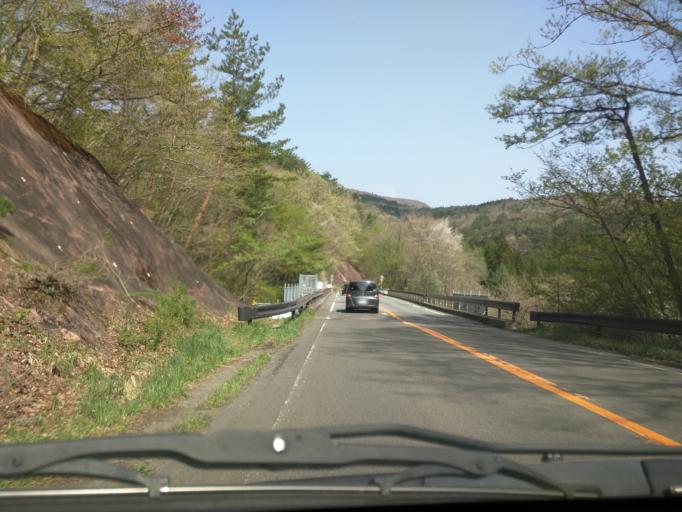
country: JP
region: Fukushima
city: Nihommatsu
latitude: 37.6015
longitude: 140.3718
